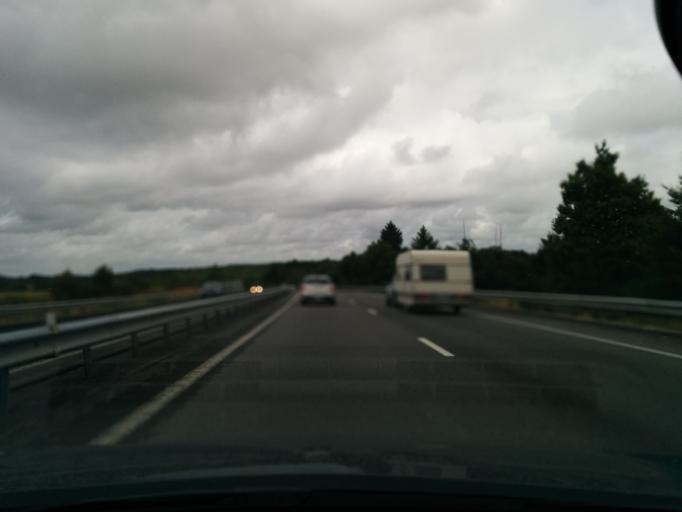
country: FR
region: Limousin
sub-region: Departement de la Haute-Vienne
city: Saint-Germain-les-Belles
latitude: 45.5163
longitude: 1.5168
